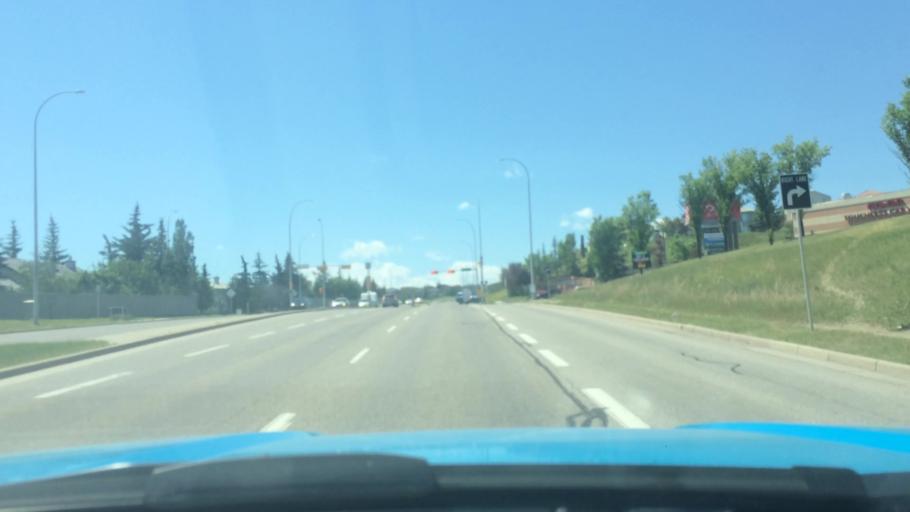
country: CA
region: Alberta
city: Calgary
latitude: 51.1409
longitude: -114.1303
